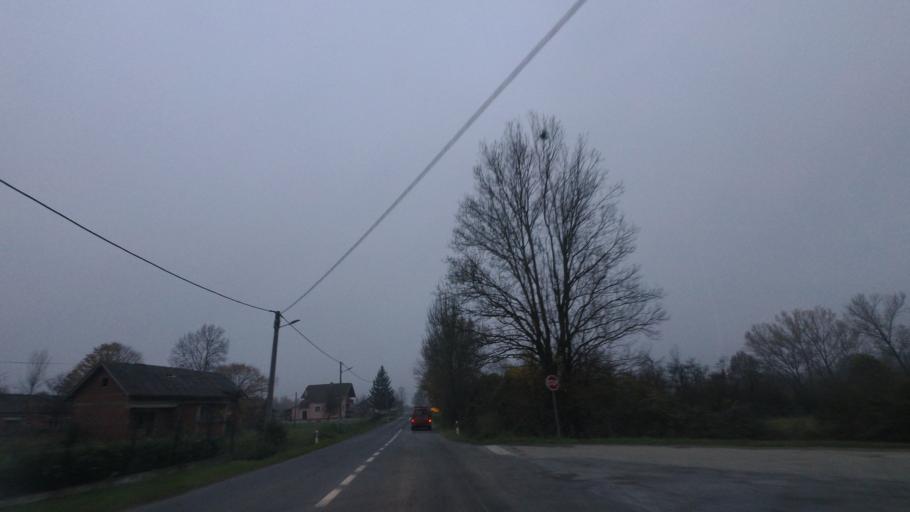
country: HR
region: Sisacko-Moslavacka
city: Petrinja
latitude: 45.4636
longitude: 16.2532
